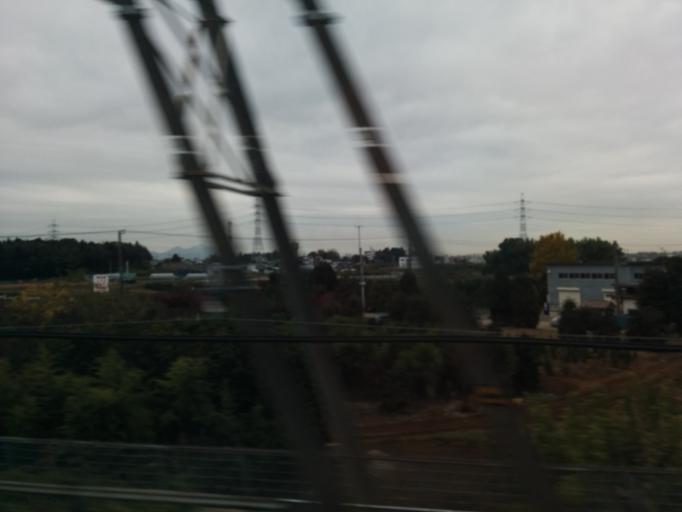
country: JP
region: Kanagawa
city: Minami-rinkan
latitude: 35.4162
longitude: 139.4295
